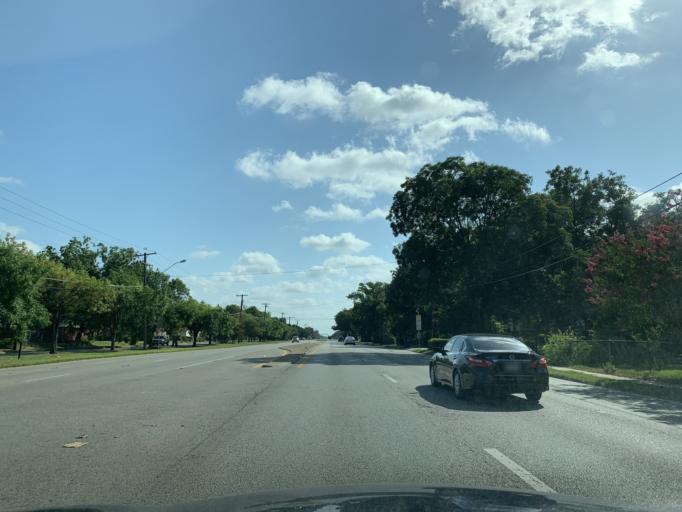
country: US
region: Texas
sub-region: Dallas County
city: Hutchins
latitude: 32.6874
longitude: -96.7868
